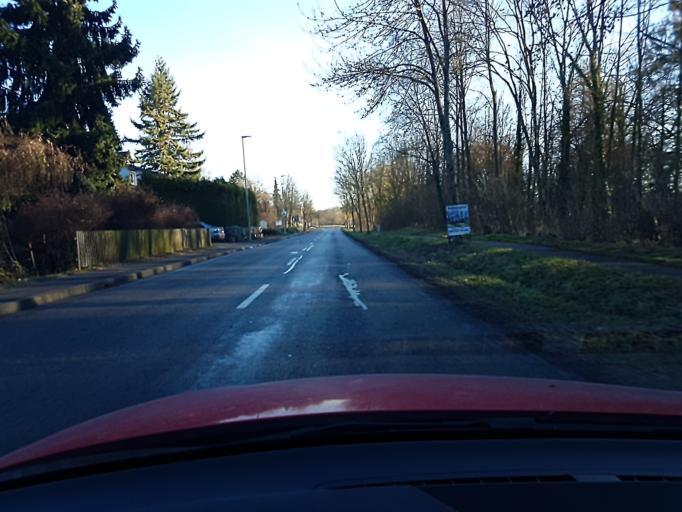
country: DE
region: Baden-Wuerttemberg
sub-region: Regierungsbezirk Stuttgart
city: Freudental
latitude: 49.0096
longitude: 9.0645
